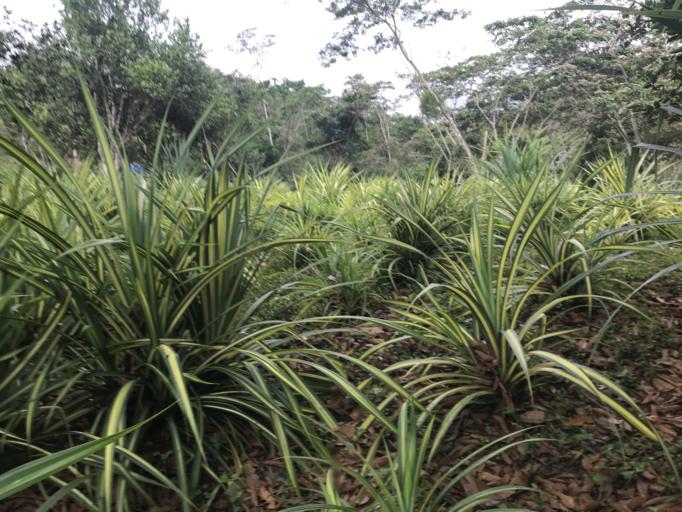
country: PE
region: Pasco
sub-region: Provincia de Oxapampa
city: Villa Rica
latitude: -10.8310
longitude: -75.2921
